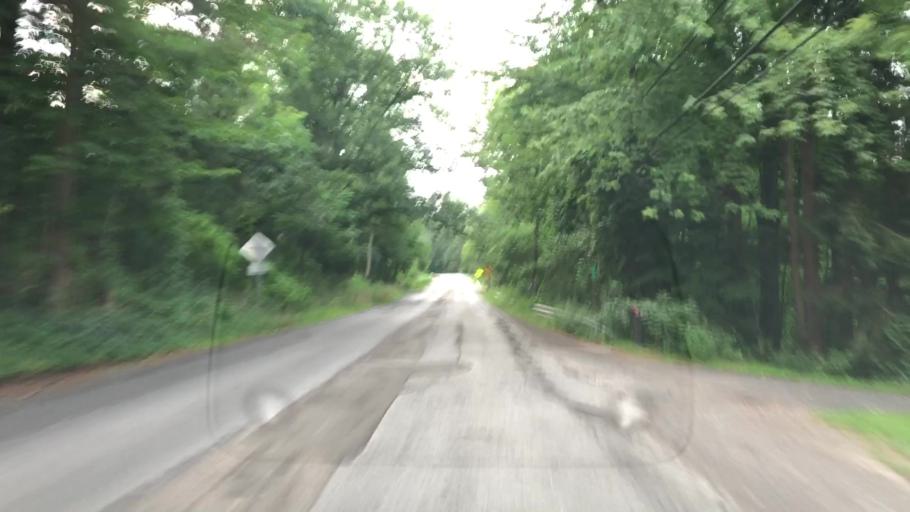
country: US
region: New York
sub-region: Erie County
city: East Aurora
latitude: 42.7857
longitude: -78.6048
